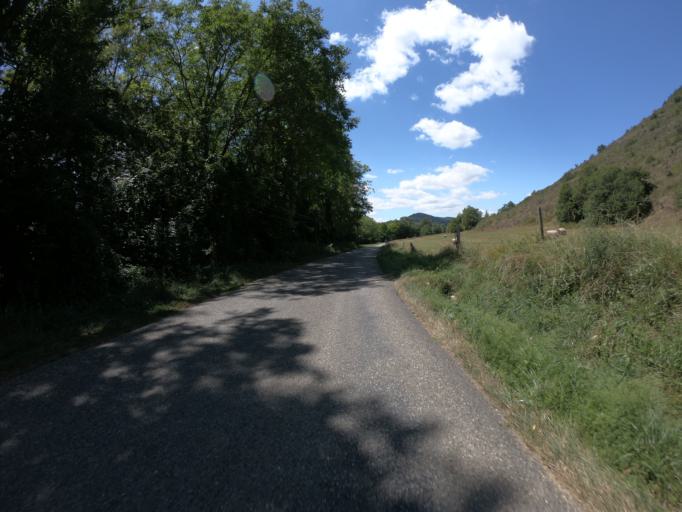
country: FR
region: Midi-Pyrenees
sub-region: Departement de l'Ariege
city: Mirepoix
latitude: 43.0485
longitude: 1.7963
